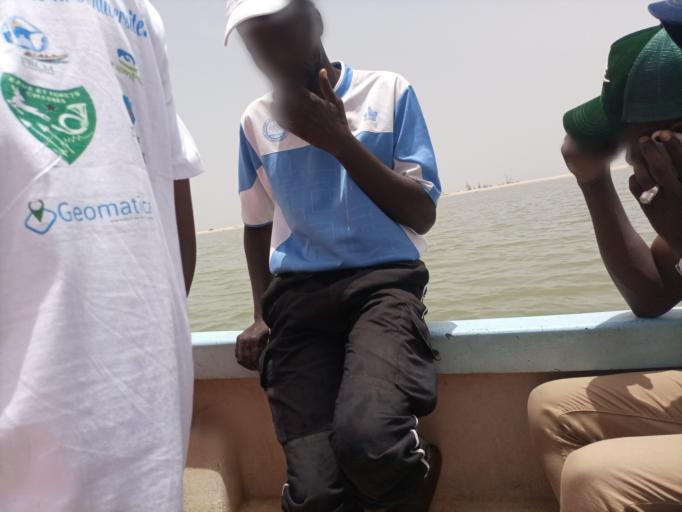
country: SN
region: Saint-Louis
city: Saint-Louis
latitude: 15.8614
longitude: -16.5159
